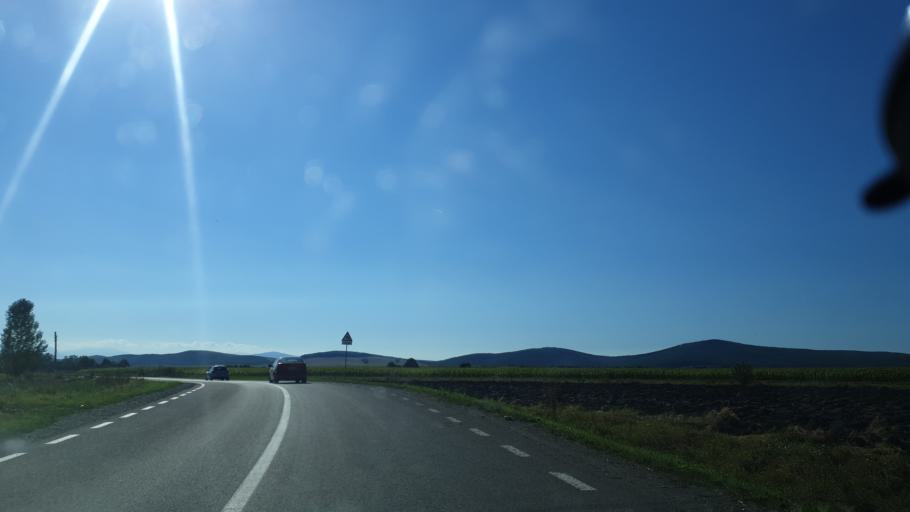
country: RO
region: Covasna
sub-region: Comuna Ilieni
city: Ilieni
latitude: 45.7887
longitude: 25.7632
